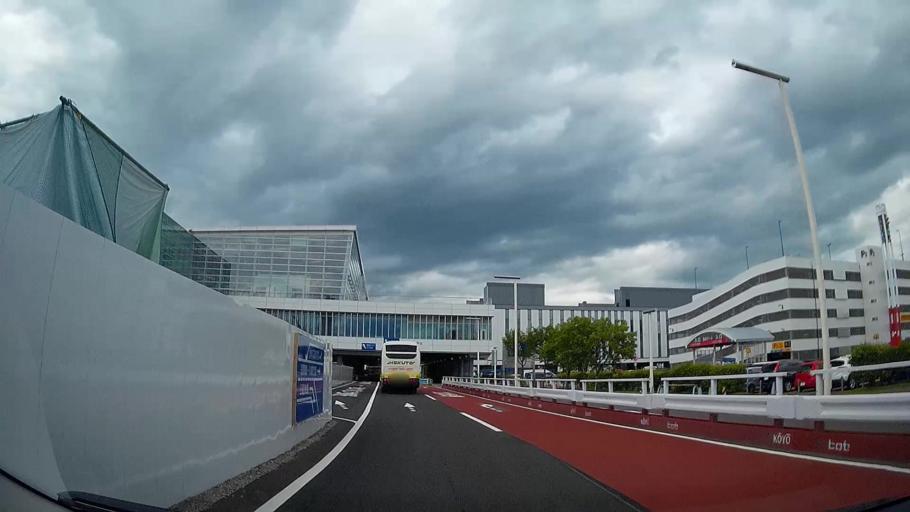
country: JP
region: Hokkaido
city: Chitose
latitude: 42.7860
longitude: 141.6771
